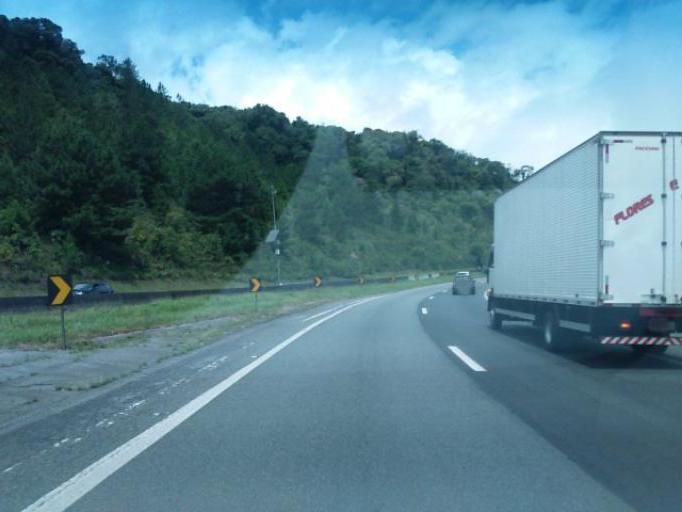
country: BR
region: Parana
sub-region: Antonina
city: Antonina
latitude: -25.0828
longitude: -48.6123
